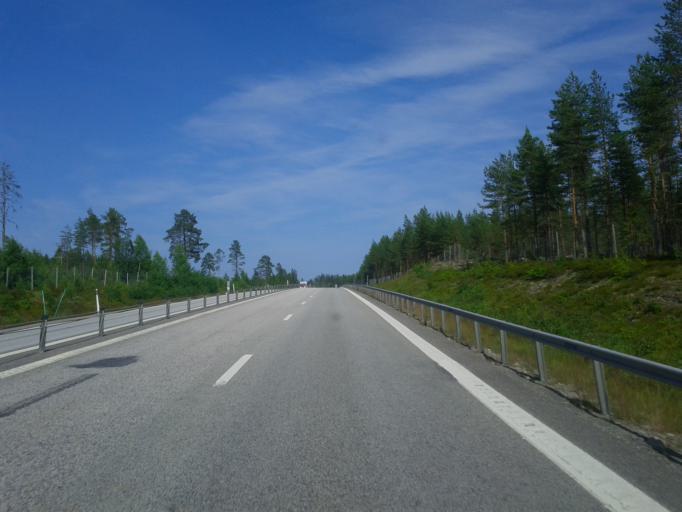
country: SE
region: Vaesterbotten
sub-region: Umea Kommun
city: Hoernefors
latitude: 63.6452
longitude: 19.9346
